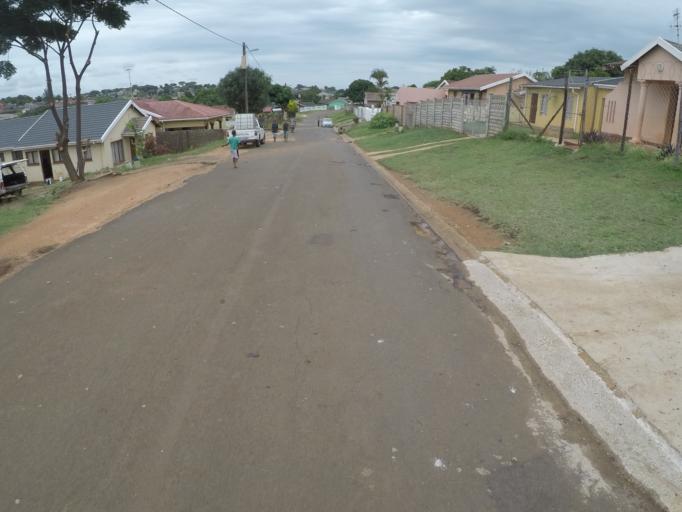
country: ZA
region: KwaZulu-Natal
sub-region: uThungulu District Municipality
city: Empangeni
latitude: -28.7762
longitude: 31.8526
